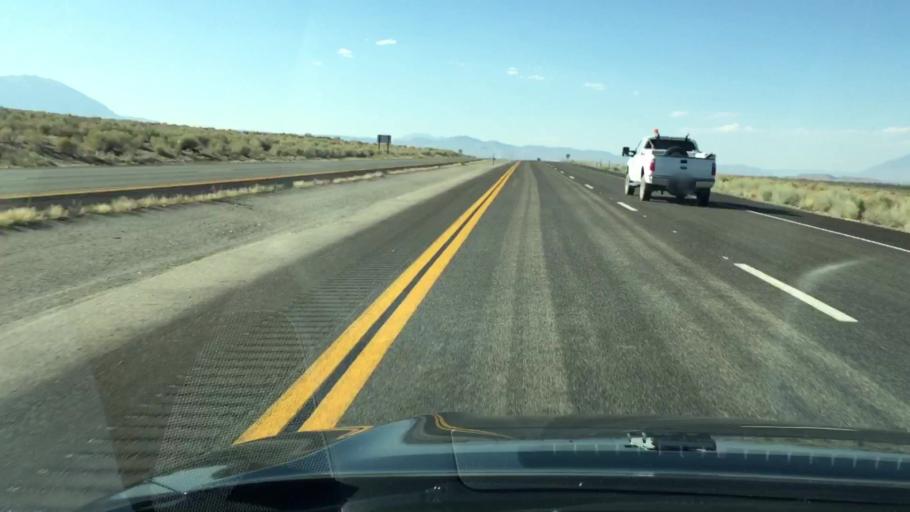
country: US
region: California
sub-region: Inyo County
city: Bishop
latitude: 37.3060
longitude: -118.3812
